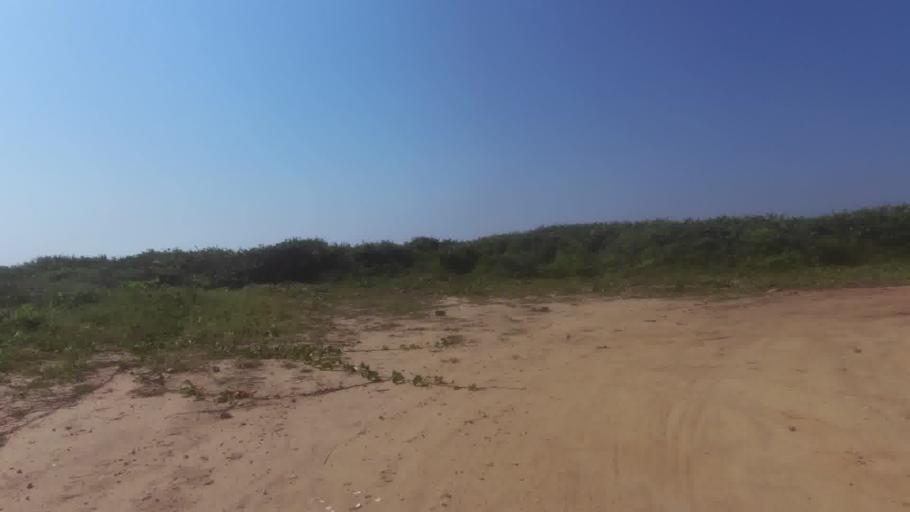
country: BR
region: Espirito Santo
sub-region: Marataizes
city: Marataizes
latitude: -21.0767
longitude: -40.8390
